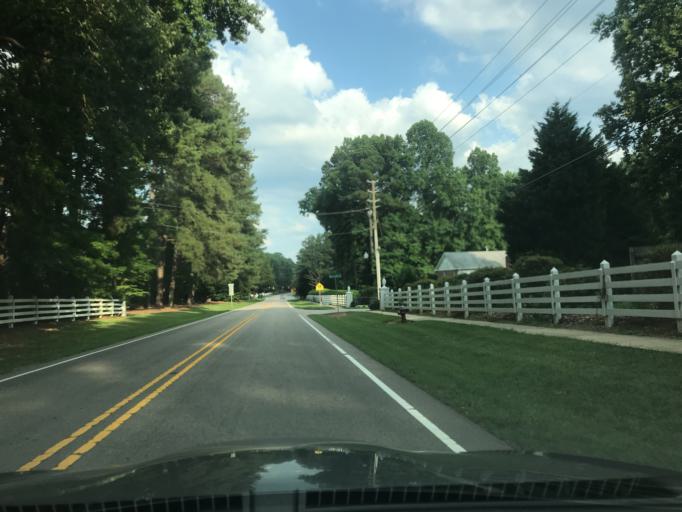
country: US
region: North Carolina
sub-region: Wake County
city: Cary
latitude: 35.8948
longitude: -78.7198
